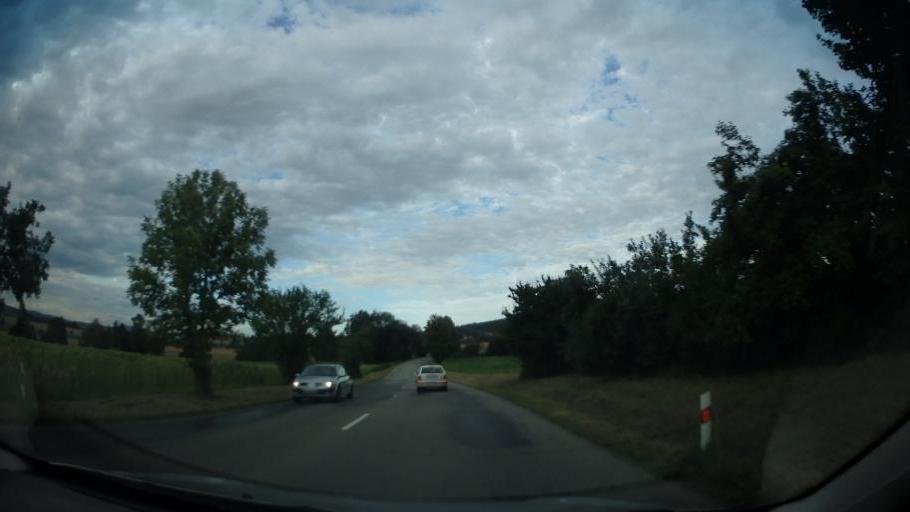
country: CZ
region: South Moravian
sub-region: Okres Blansko
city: Boskovice
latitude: 49.5422
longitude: 16.7033
